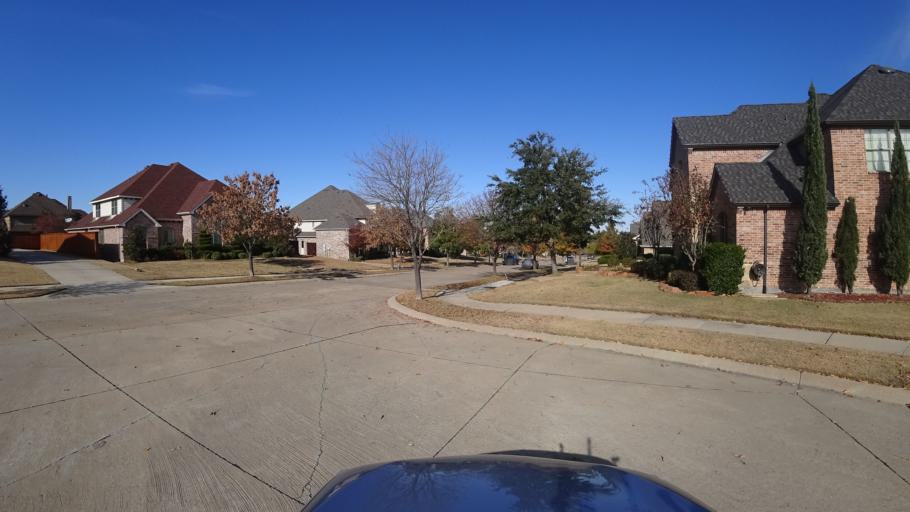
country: US
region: Texas
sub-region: Denton County
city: The Colony
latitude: 33.0273
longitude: -96.9078
